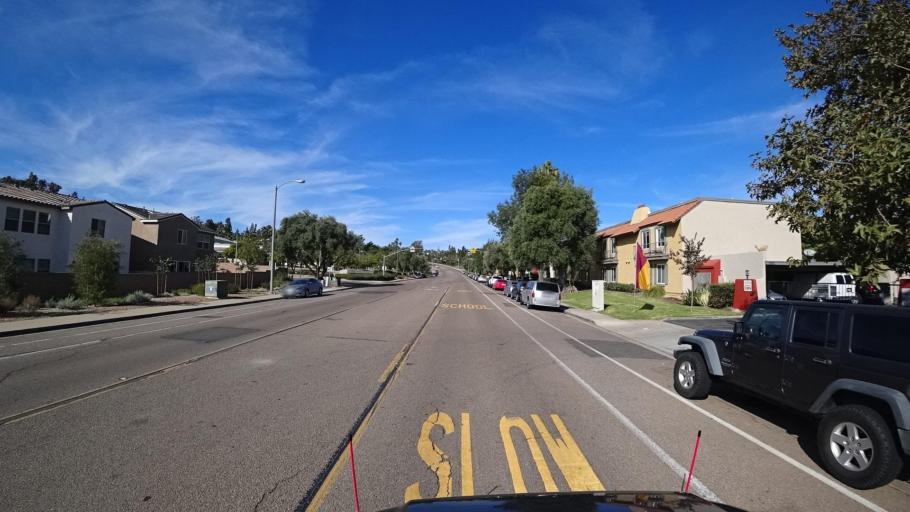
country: US
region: California
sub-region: San Diego County
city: Spring Valley
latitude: 32.7313
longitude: -116.9733
